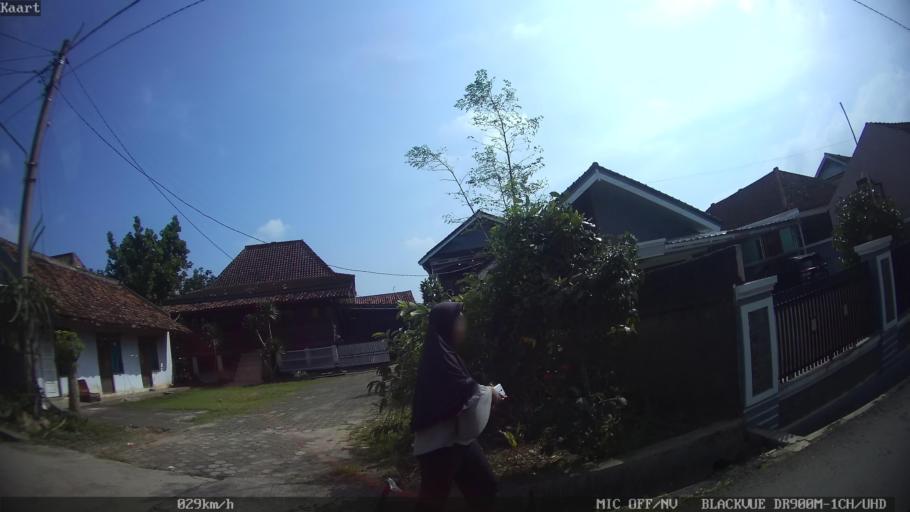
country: ID
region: Lampung
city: Kedaton
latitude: -5.3657
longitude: 105.2331
